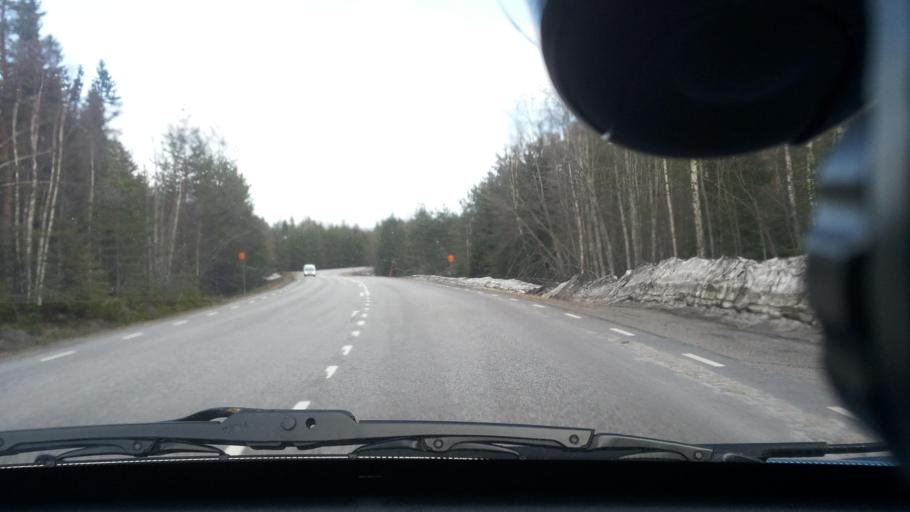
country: SE
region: Norrbotten
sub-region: Lulea Kommun
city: Gammelstad
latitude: 65.5876
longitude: 22.0099
